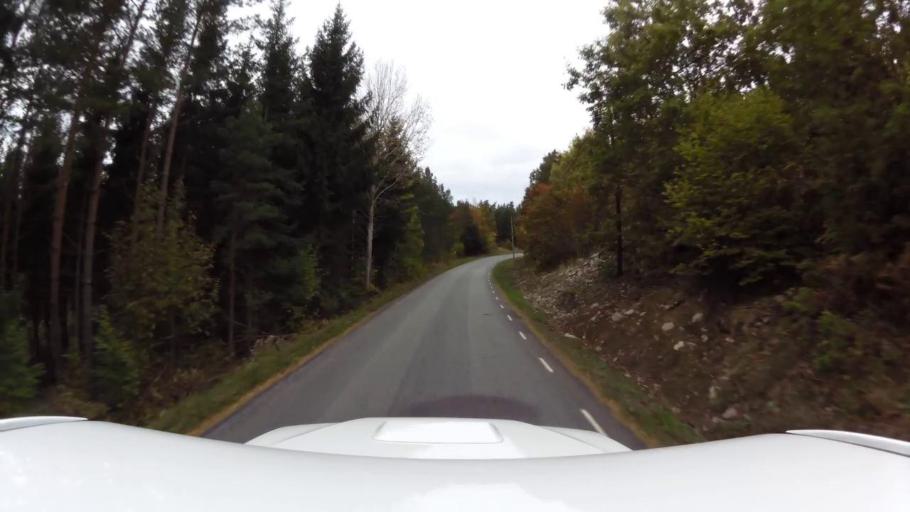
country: SE
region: OEstergoetland
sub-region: Linkopings Kommun
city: Ljungsbro
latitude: 58.5417
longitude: 15.4143
